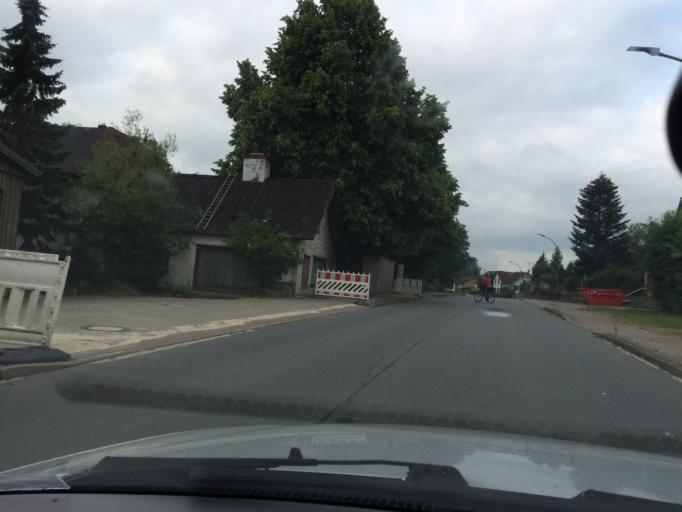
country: DE
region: Schleswig-Holstein
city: Oeversee
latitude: 54.6948
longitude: 9.4272
